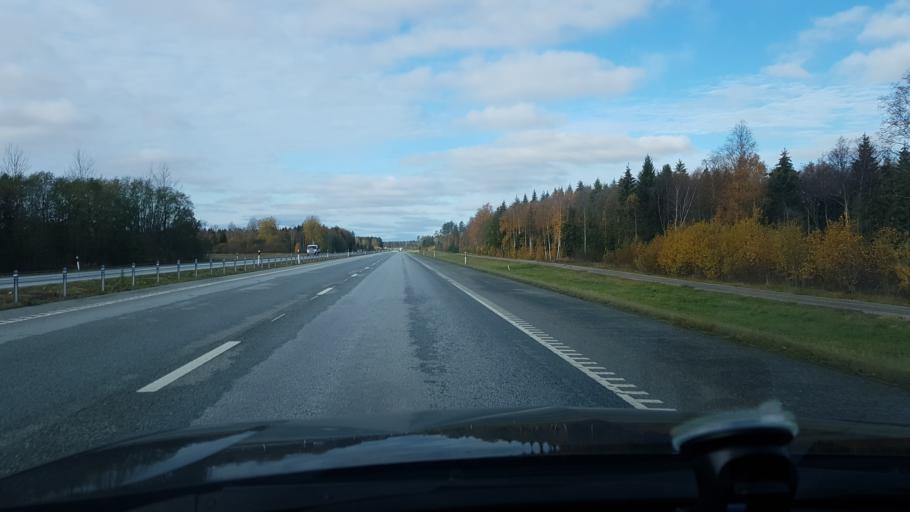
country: EE
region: Laeaene-Virumaa
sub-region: Kadrina vald
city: Kadrina
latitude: 59.4523
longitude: 26.0605
